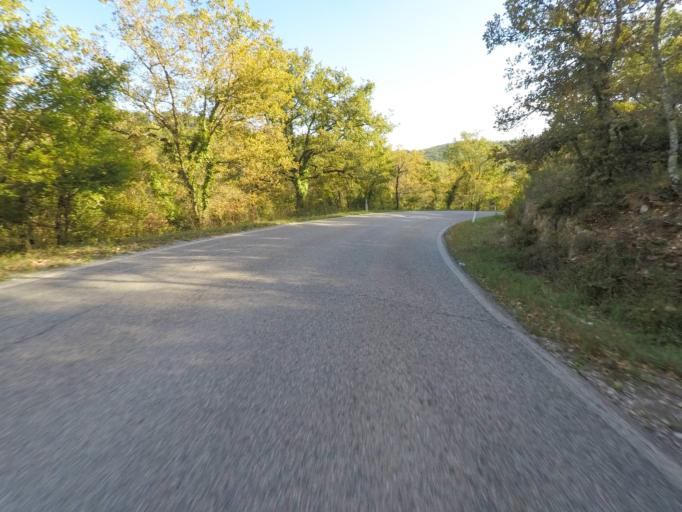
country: IT
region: Tuscany
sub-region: Provincia di Siena
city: Radda in Chianti
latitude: 43.4737
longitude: 11.3743
